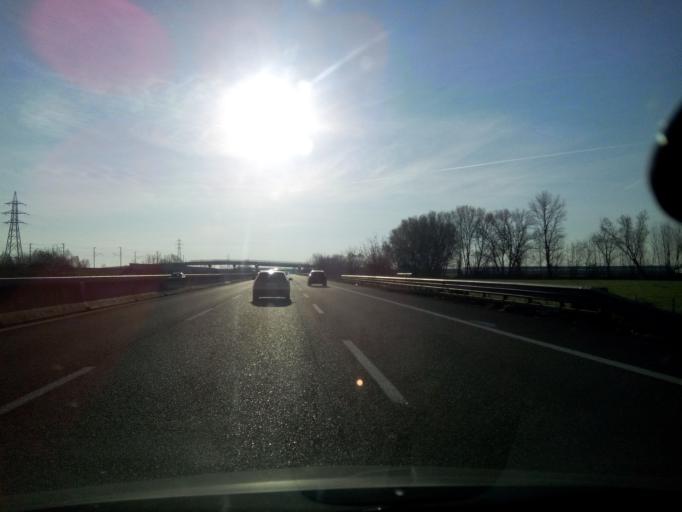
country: IT
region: Emilia-Romagna
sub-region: Provincia di Parma
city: Soragna
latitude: 44.8863
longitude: 10.1088
